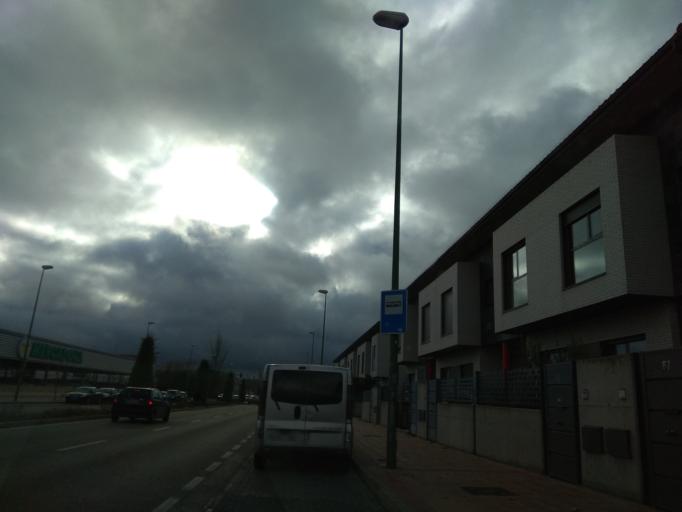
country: ES
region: Castille and Leon
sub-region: Provincia de Burgos
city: Burgos
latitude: 42.3692
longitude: -3.6569
